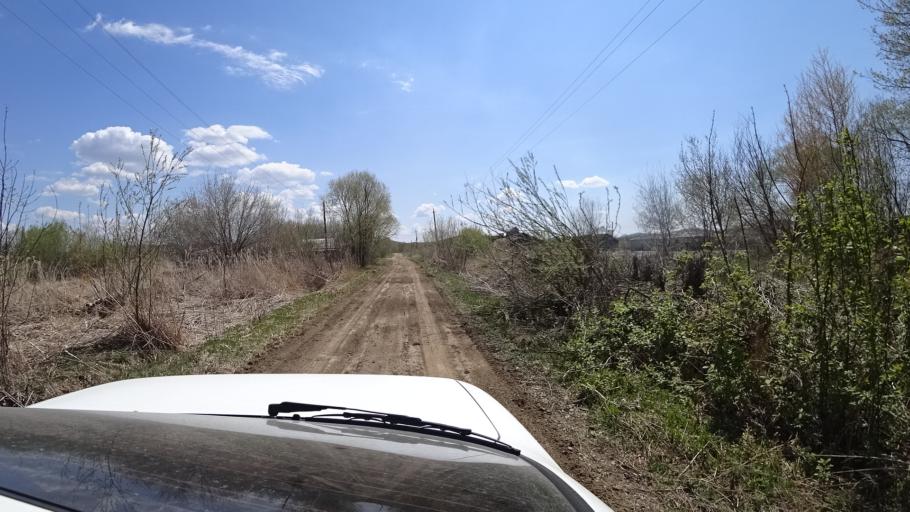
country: RU
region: Primorskiy
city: Lazo
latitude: 45.7998
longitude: 133.7607
